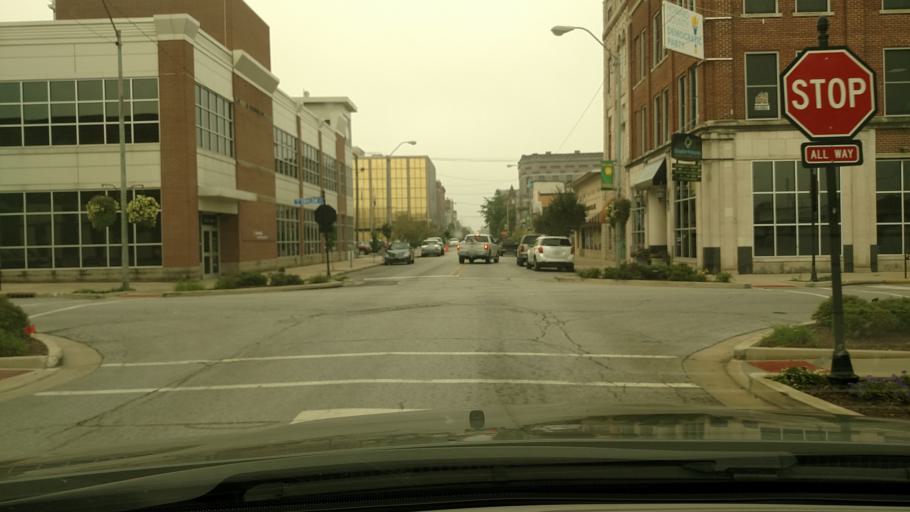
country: US
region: Indiana
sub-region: Howard County
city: Kokomo
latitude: 40.4895
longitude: -86.1313
